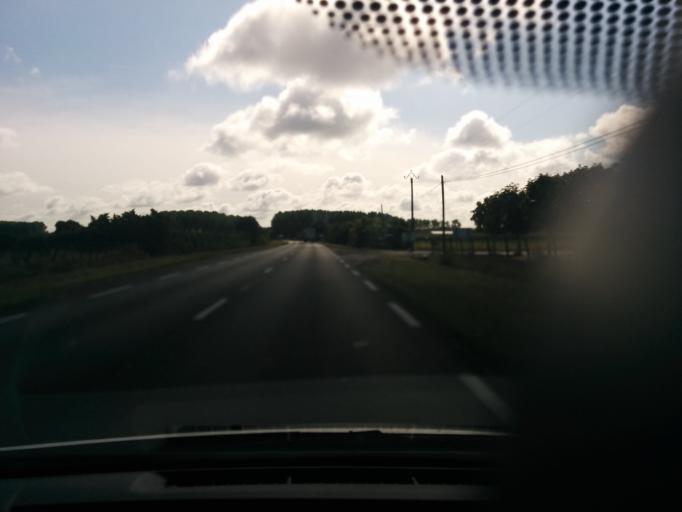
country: FR
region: Pays de la Loire
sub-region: Departement de Maine-et-Loire
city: Andard
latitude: 47.4657
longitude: -0.4251
